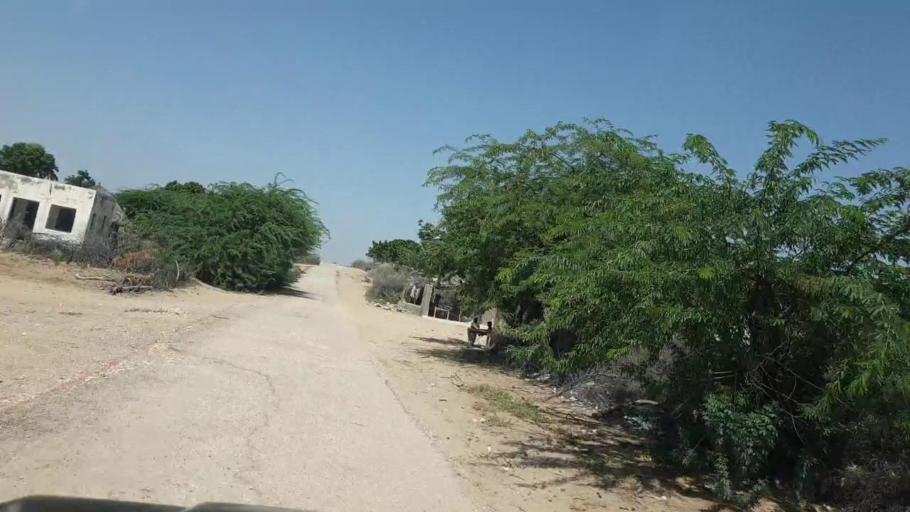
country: PK
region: Sindh
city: Chor
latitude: 25.3765
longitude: 70.3152
